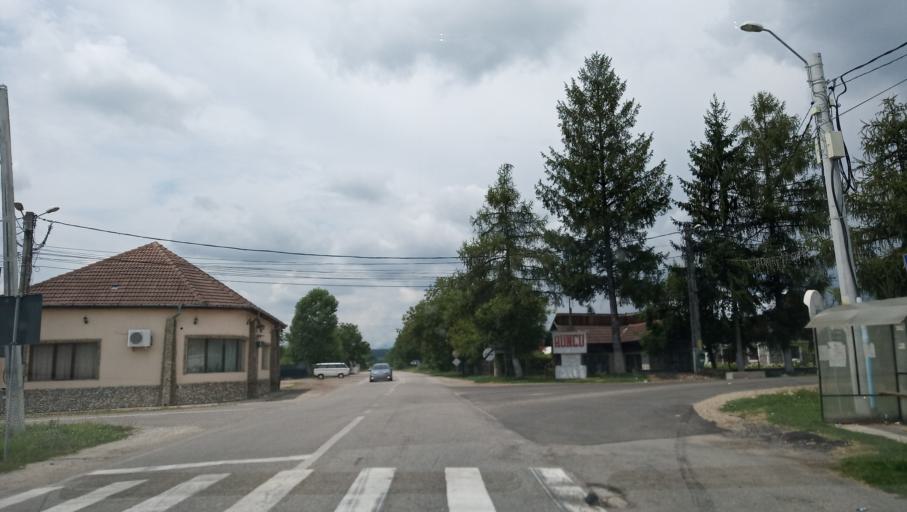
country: RO
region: Gorj
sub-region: Comuna Arcani
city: Arcani
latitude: 45.0879
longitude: 23.1527
